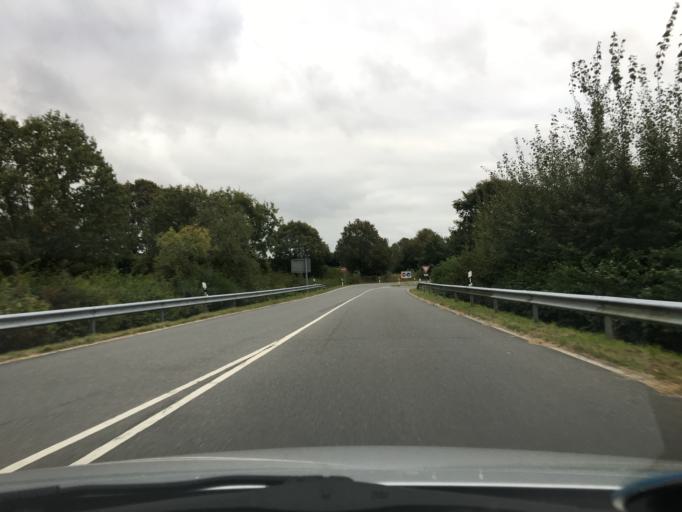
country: DE
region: Schleswig-Holstein
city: Neudorf-Bornstein
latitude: 54.4433
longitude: 9.9154
